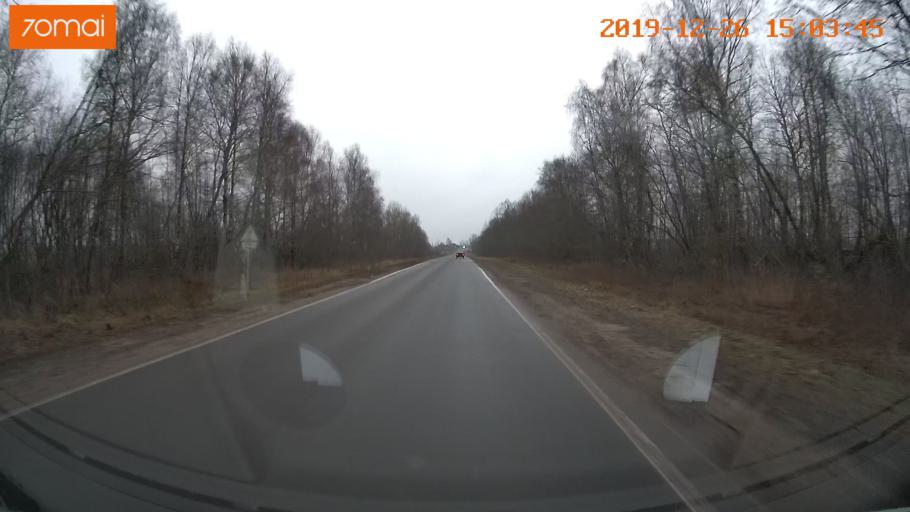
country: RU
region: Jaroslavl
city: Rybinsk
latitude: 58.2081
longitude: 38.8682
